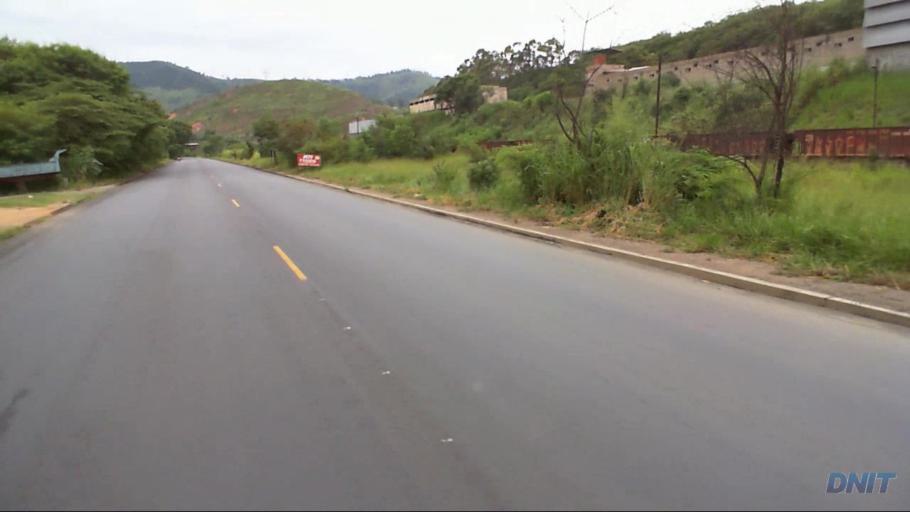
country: BR
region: Minas Gerais
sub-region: Coronel Fabriciano
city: Coronel Fabriciano
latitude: -19.5294
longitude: -42.6324
